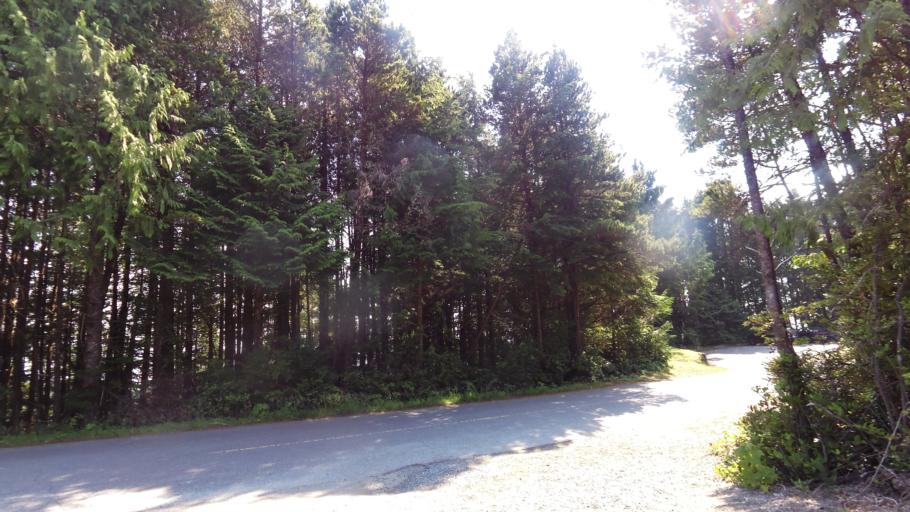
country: CA
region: British Columbia
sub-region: Regional District of Alberni-Clayoquot
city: Tofino
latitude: 49.0832
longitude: -125.8410
